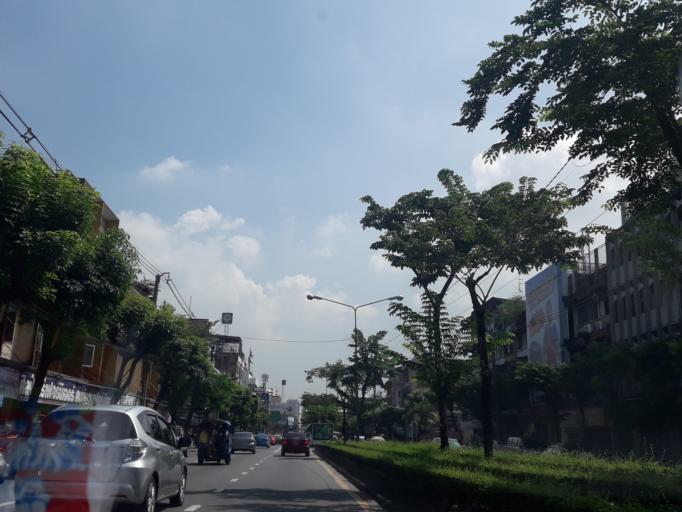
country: TH
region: Bangkok
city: Bangkok Noi
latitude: 13.7553
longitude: 100.4750
